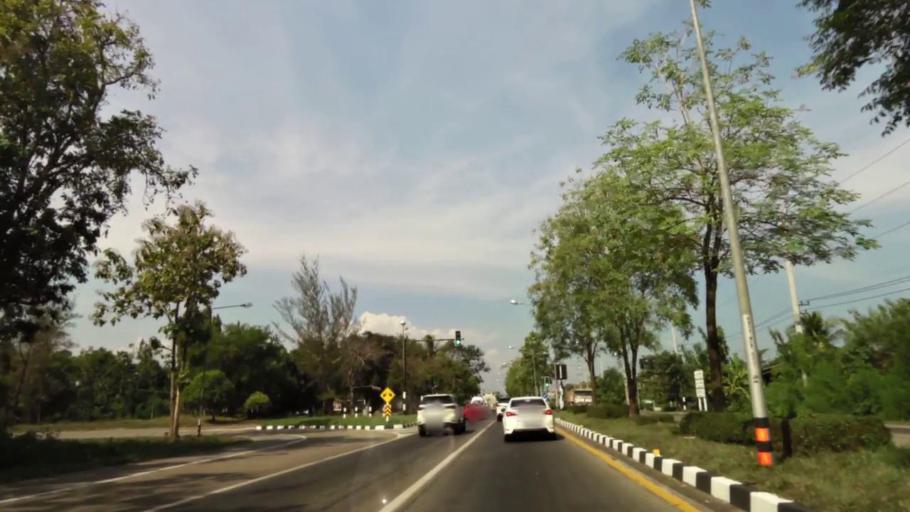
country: TH
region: Uttaradit
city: Uttaradit
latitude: 17.5869
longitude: 100.1371
